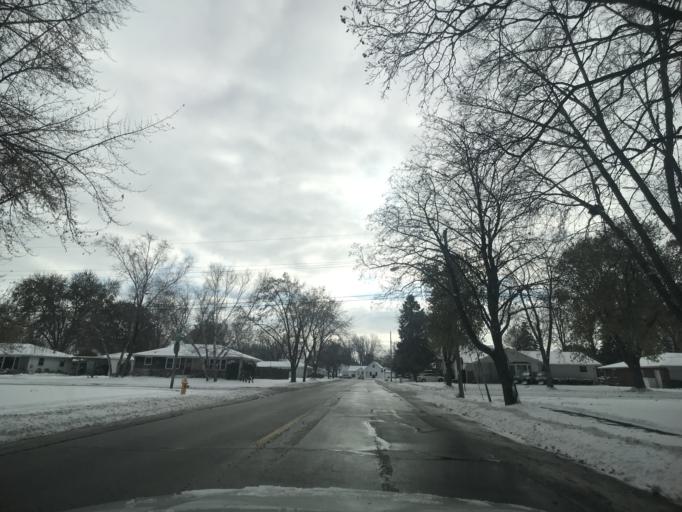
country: US
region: Wisconsin
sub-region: Brown County
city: De Pere
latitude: 44.4463
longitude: -88.0856
